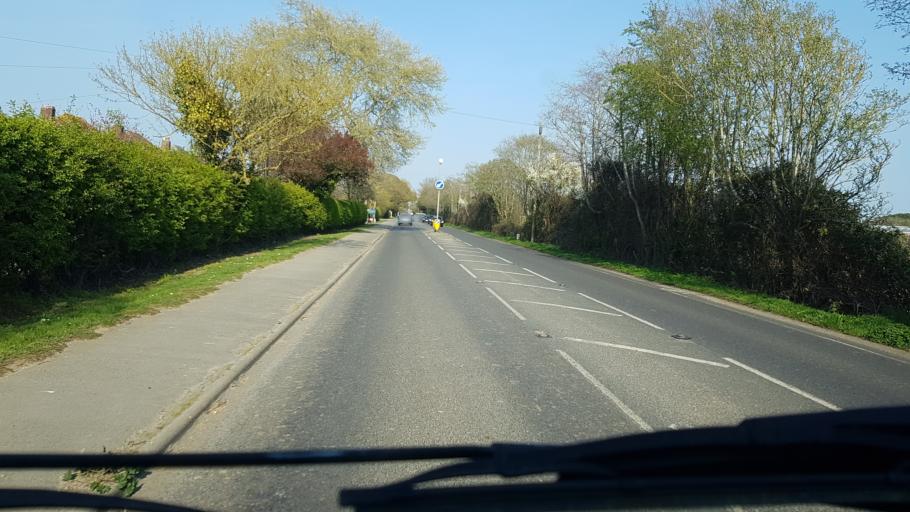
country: GB
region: England
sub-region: West Sussex
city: Birdham
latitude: 50.7925
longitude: -0.8316
